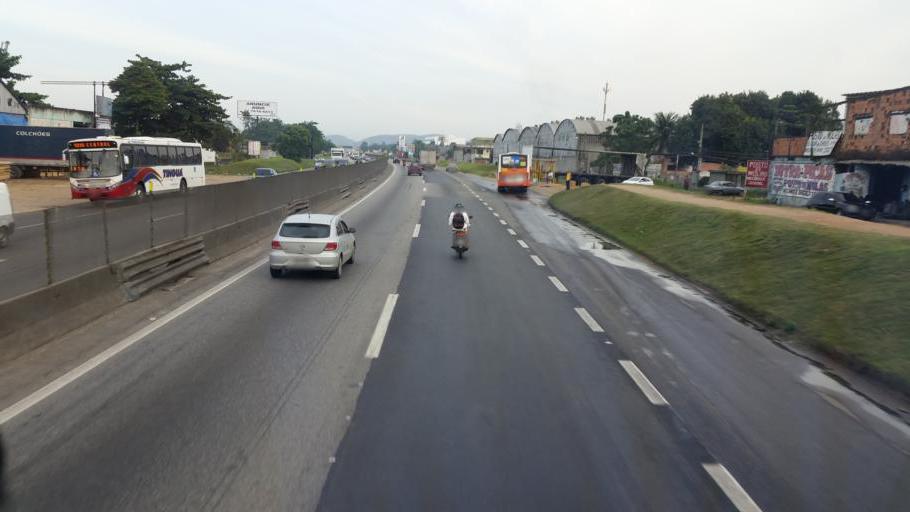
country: BR
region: Rio de Janeiro
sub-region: Nova Iguacu
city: Nova Iguacu
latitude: -22.7403
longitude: -43.4571
